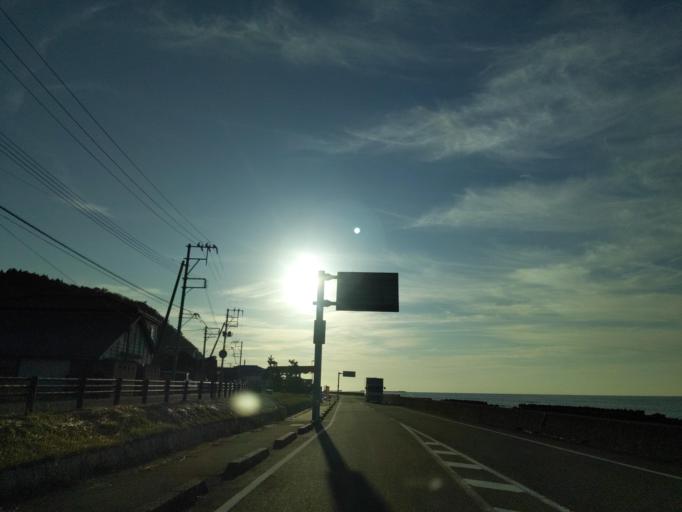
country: JP
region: Niigata
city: Nagaoka
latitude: 37.5535
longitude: 138.7056
